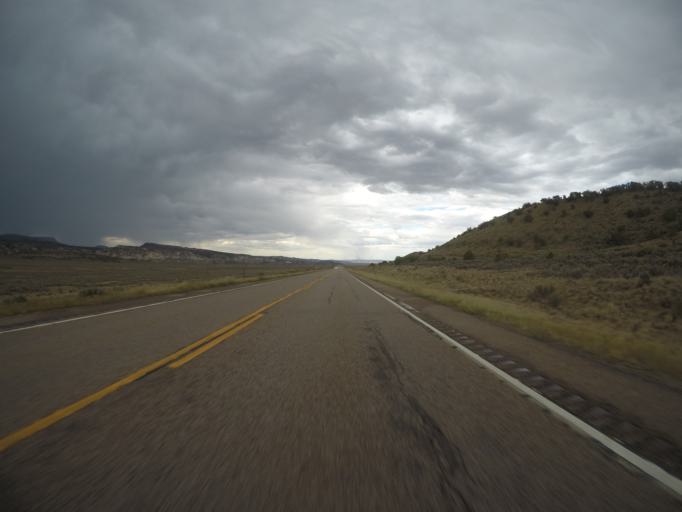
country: US
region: Colorado
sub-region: Rio Blanco County
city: Rangely
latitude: 40.2513
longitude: -108.8129
